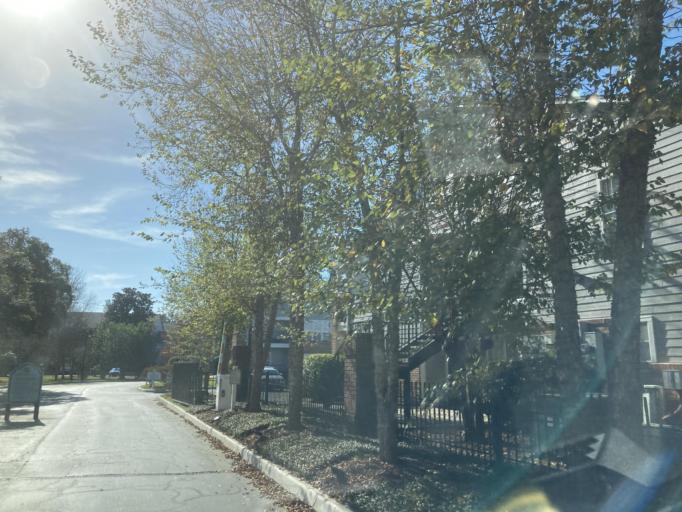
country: US
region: Mississippi
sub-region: Harrison County
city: West Gulfport
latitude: 30.3993
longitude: -89.0235
